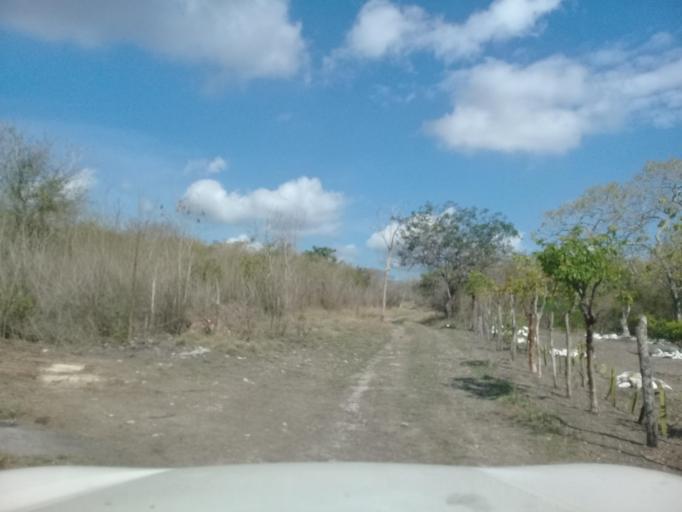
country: MX
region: Veracruz
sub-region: Emiliano Zapata
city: Plan del Rio
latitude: 19.4118
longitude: -96.6544
